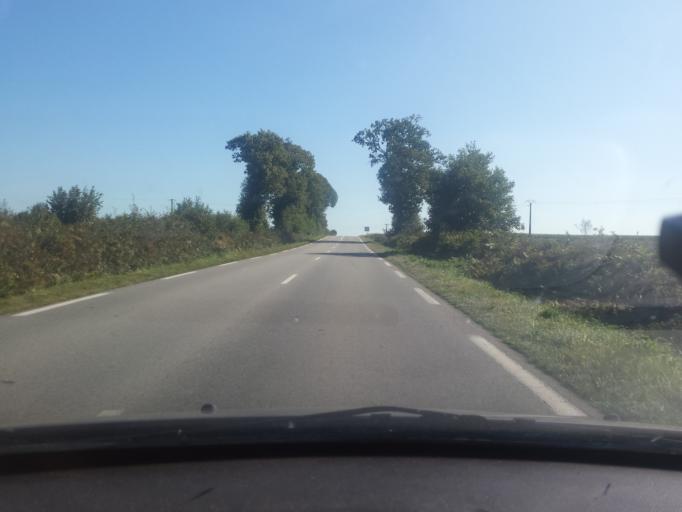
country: FR
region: Brittany
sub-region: Departement du Morbihan
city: Saint-Thuriau
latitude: 48.0150
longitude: -2.9075
